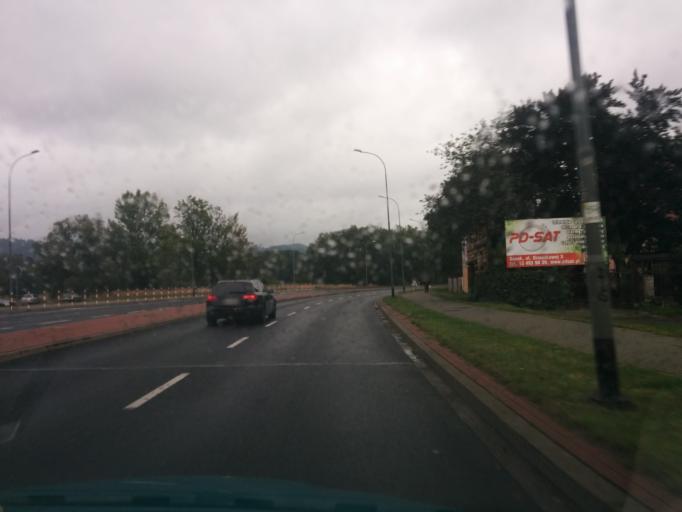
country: PL
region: Subcarpathian Voivodeship
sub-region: Powiat sanocki
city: Sanok
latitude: 49.5660
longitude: 22.2059
